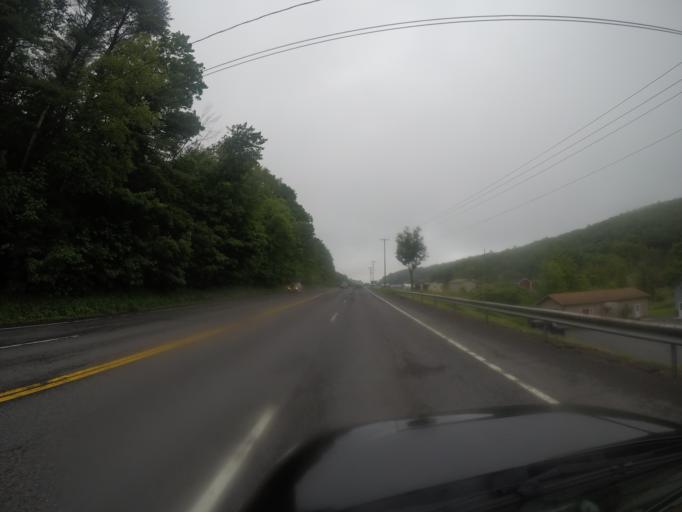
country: US
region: New York
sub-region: Ulster County
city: Hurley
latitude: 41.9624
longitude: -74.0603
